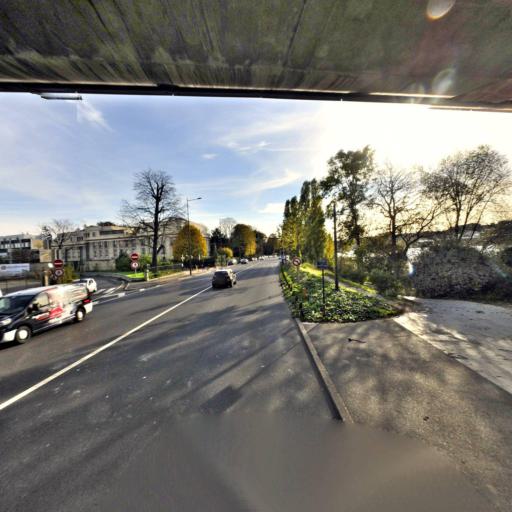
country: FR
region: Ile-de-France
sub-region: Departement des Hauts-de-Seine
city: Suresnes
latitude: 48.8485
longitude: 2.2273
